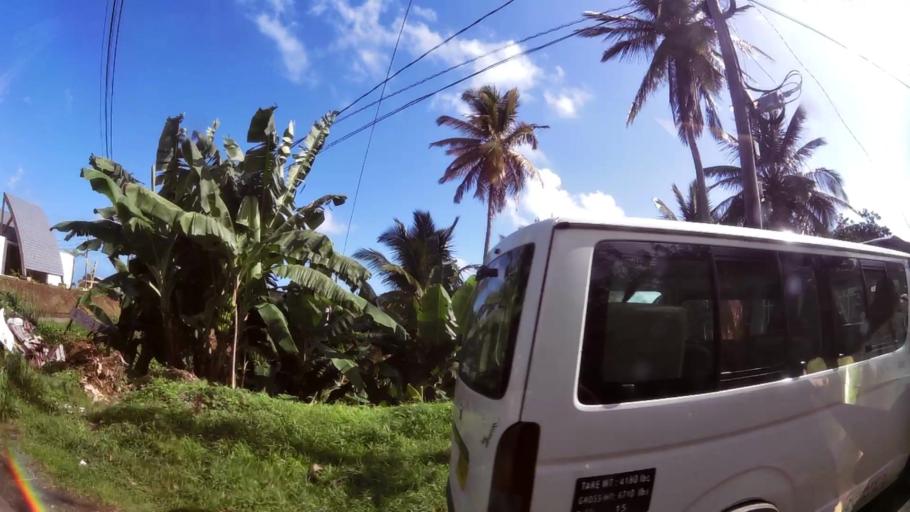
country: DM
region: Saint David
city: Castle Bruce
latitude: 15.4898
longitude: -61.2531
